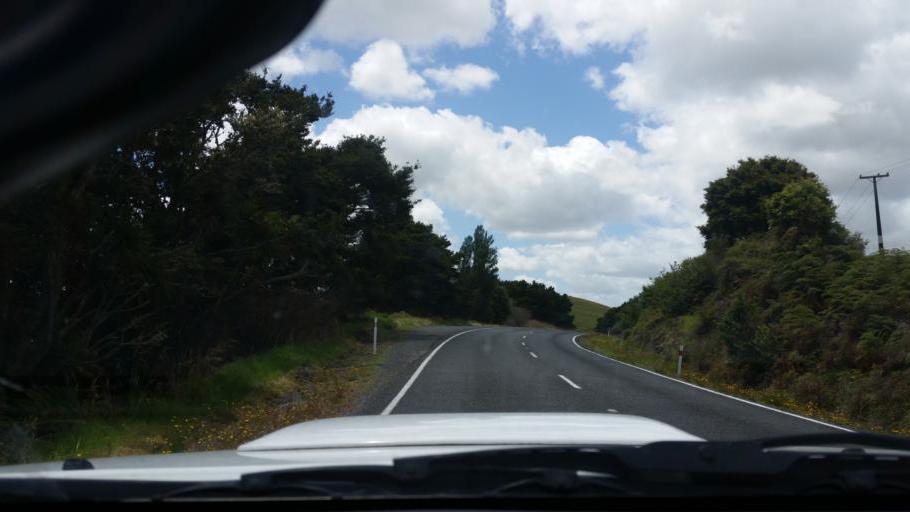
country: NZ
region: Northland
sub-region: Whangarei
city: Ruakaka
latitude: -36.0539
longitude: 174.2746
